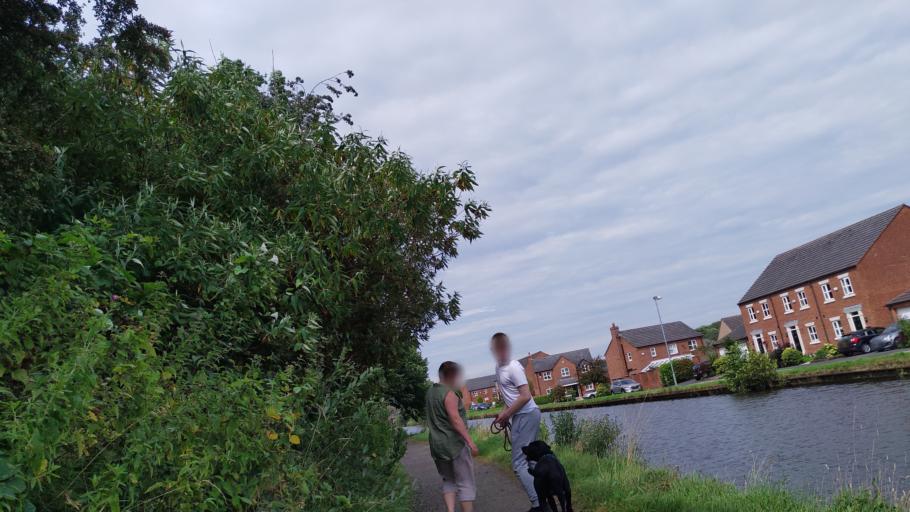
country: GB
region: England
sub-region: Lancashire
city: Chorley
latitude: 53.6526
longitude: -2.6137
